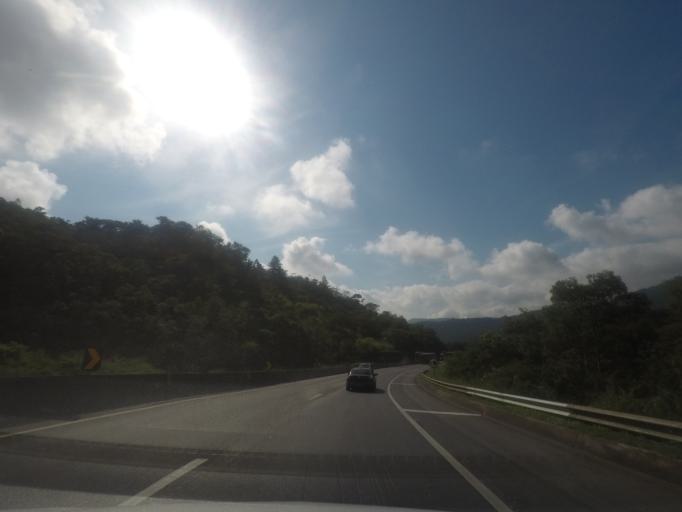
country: BR
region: Parana
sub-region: Antonina
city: Antonina
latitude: -25.5614
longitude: -48.8120
